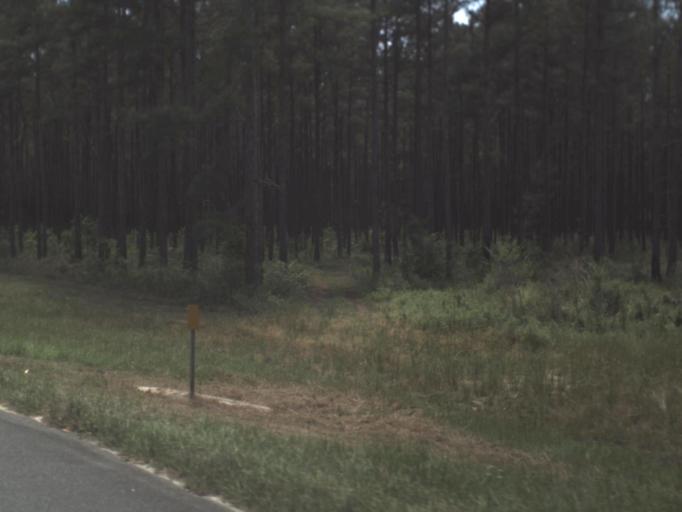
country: US
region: Florida
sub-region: Gulf County
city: Wewahitchka
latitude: 30.2327
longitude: -85.2071
